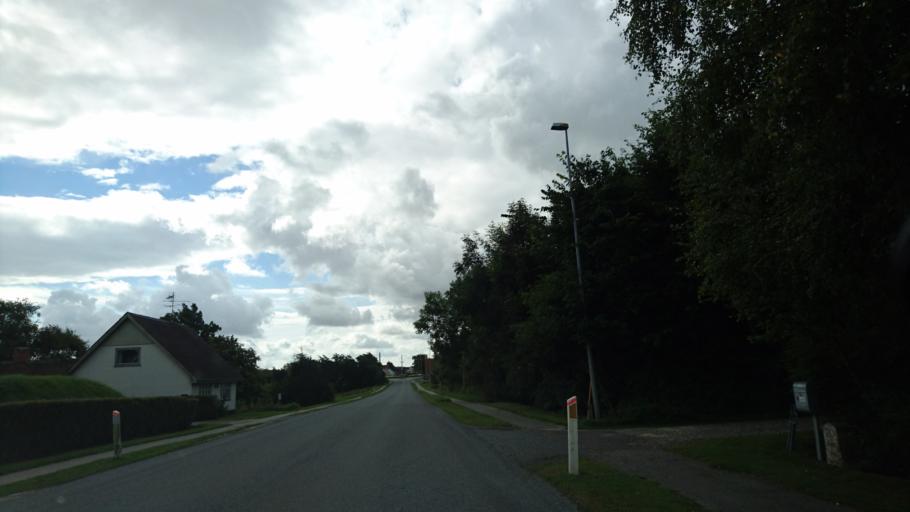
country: DK
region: North Denmark
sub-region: Hjorring Kommune
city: Tars
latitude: 57.3469
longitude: 10.2304
